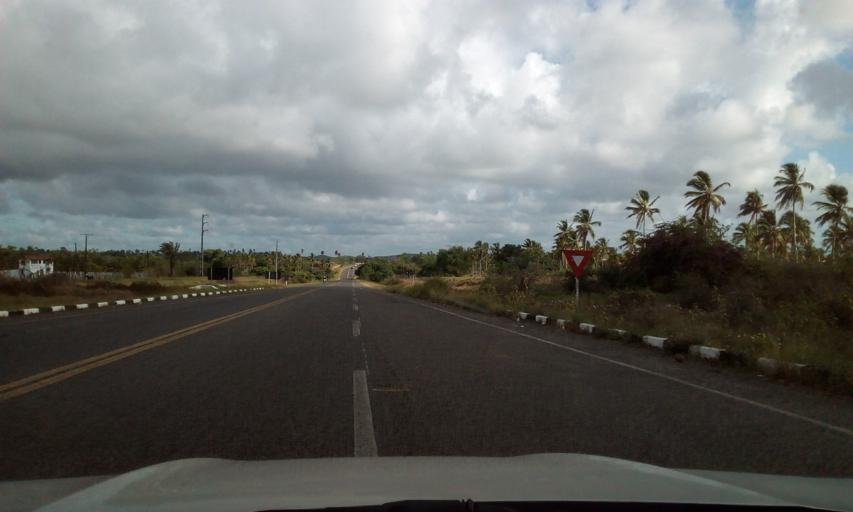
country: BR
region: Bahia
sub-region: Conde
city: Conde
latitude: -11.8242
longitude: -37.6354
